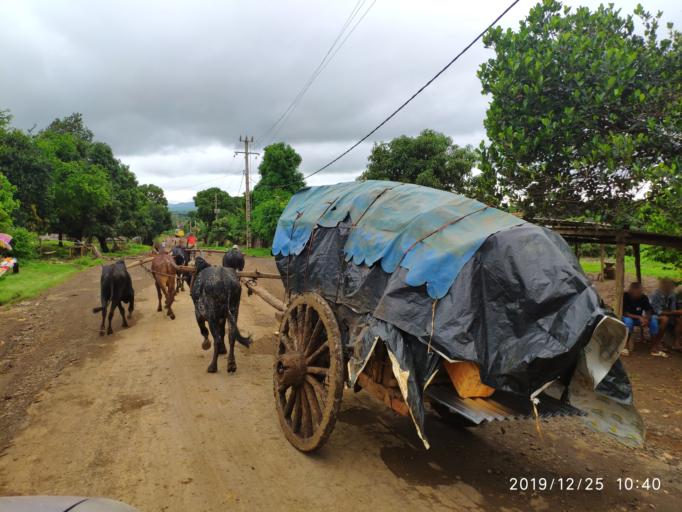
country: MG
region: Diana
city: Sadjoavato
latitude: -12.7531
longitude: 49.2369
